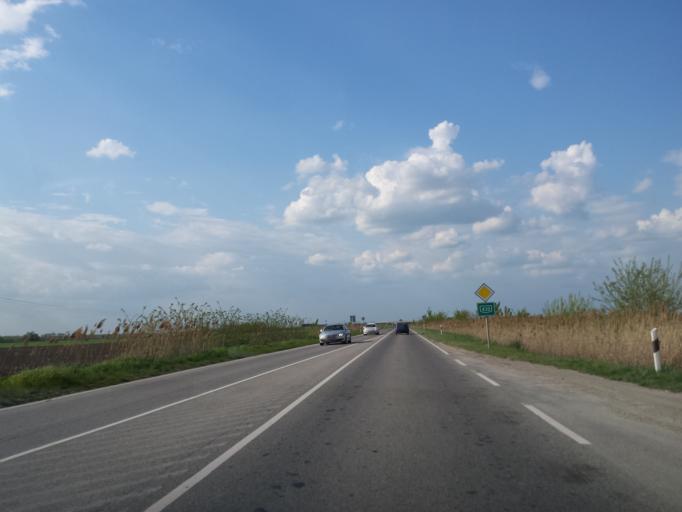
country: HU
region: Csongrad
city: Mako
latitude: 46.2552
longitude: 20.4848
